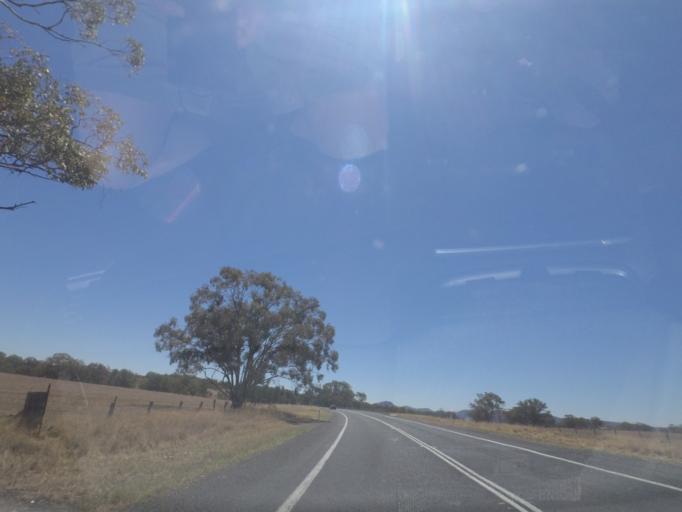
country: AU
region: New South Wales
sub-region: Warrumbungle Shire
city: Coonabarabran
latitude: -31.4172
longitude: 149.2110
